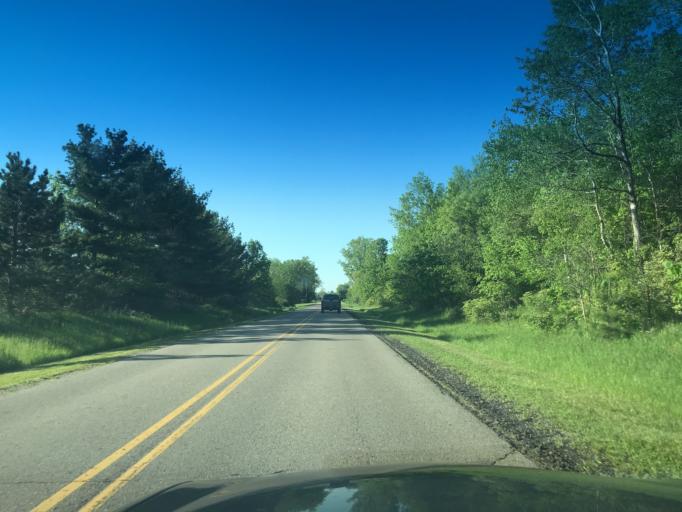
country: US
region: Michigan
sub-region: Ingham County
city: Mason
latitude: 42.5554
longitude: -84.4530
